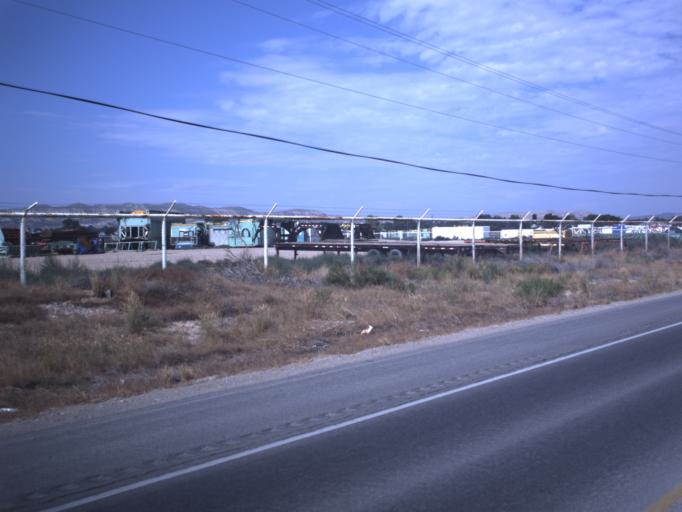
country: US
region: Utah
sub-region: Uintah County
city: Naples
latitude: 40.4003
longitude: -109.4664
